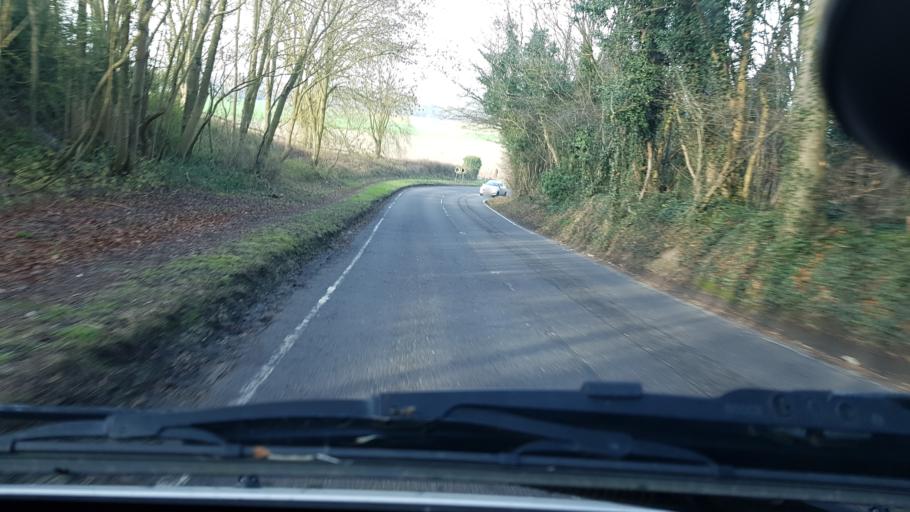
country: GB
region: England
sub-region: Surrey
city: Normandy
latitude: 51.2282
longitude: -0.6642
